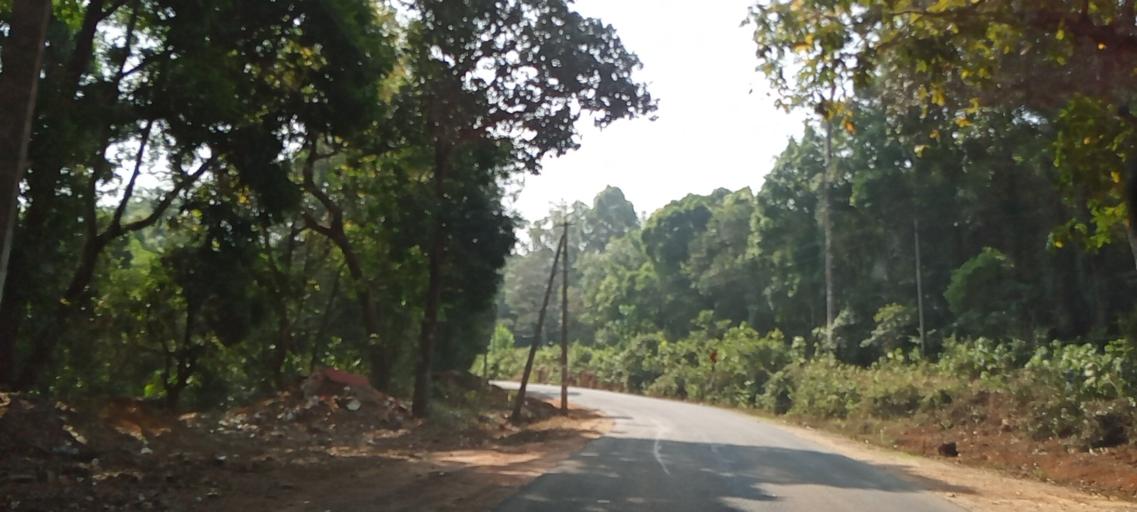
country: IN
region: Karnataka
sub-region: Udupi
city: Someshwar
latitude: 13.5331
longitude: 74.9169
